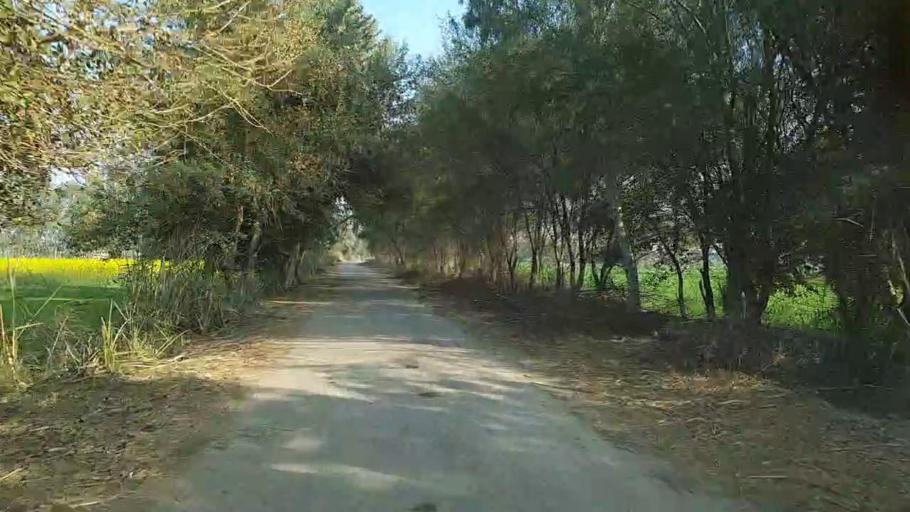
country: PK
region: Sindh
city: Mirpur Mathelo
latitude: 27.8766
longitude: 69.6178
